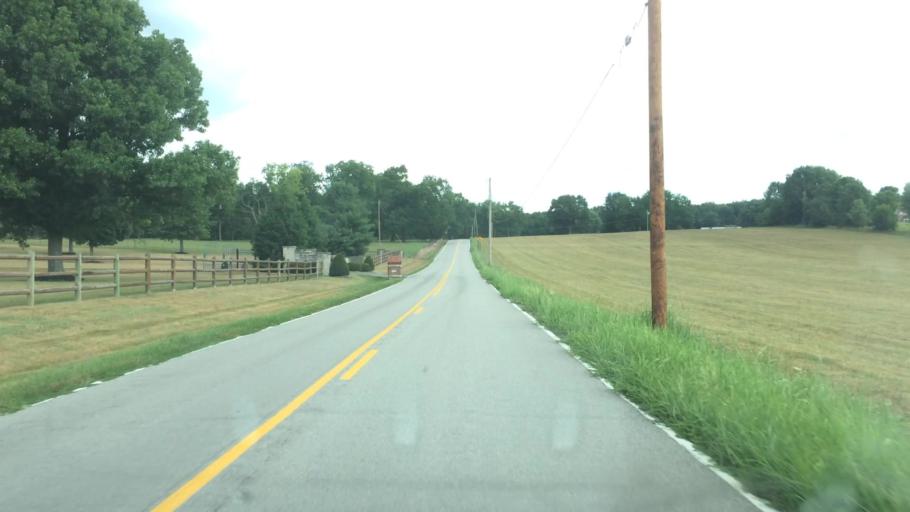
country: US
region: Missouri
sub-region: Greene County
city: Strafford
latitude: 37.1869
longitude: -93.1846
